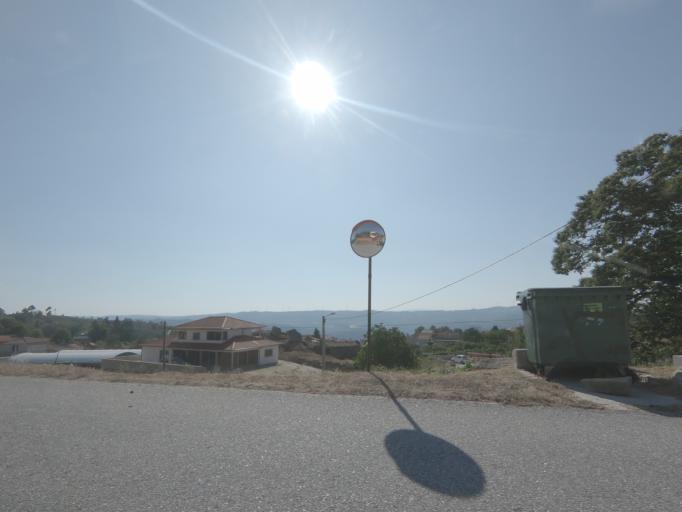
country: PT
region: Viseu
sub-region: Tabuaco
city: Tabuaco
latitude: 41.0489
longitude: -7.5676
